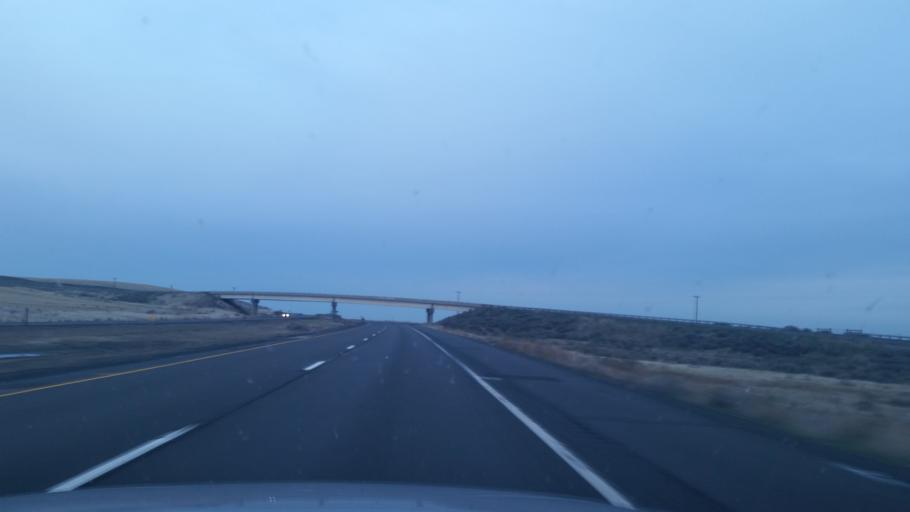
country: US
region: Washington
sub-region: Adams County
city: Ritzville
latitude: 47.2578
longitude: -118.0821
